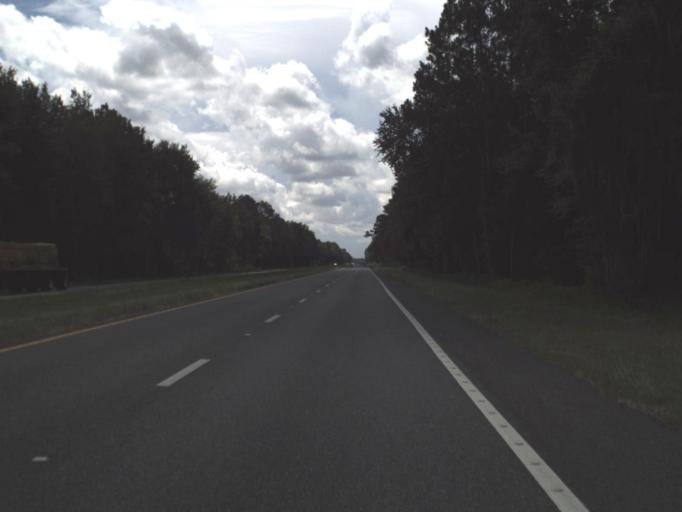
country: US
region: Florida
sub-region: Taylor County
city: Perry
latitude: 30.2129
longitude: -83.6664
